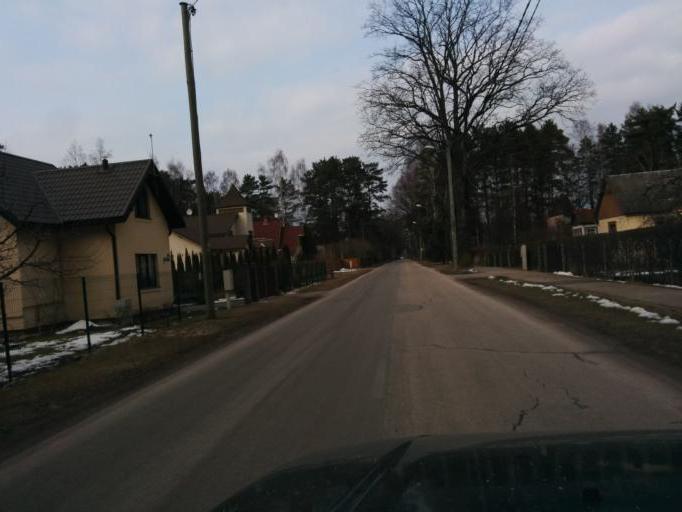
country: LV
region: Jurmala
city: Jurmala
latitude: 56.9510
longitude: 23.7251
